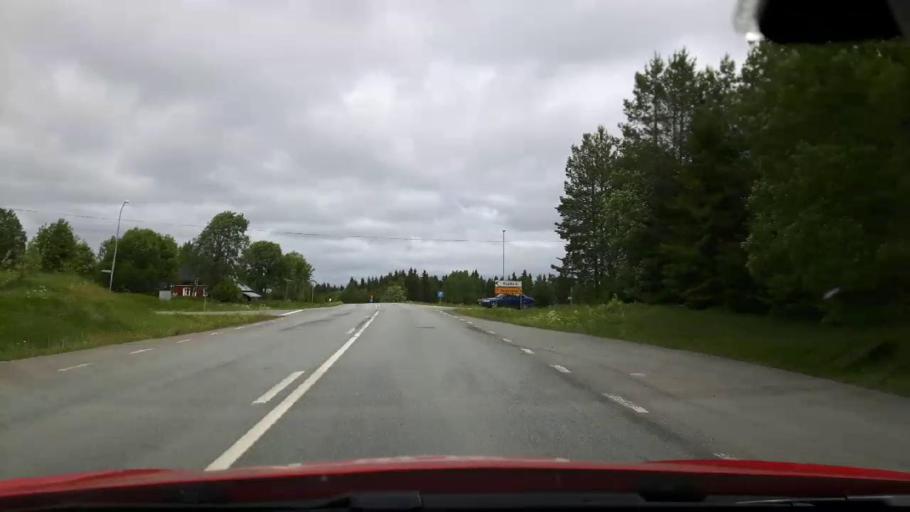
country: SE
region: Jaemtland
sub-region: Krokoms Kommun
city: Krokom
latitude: 63.3618
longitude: 14.5032
